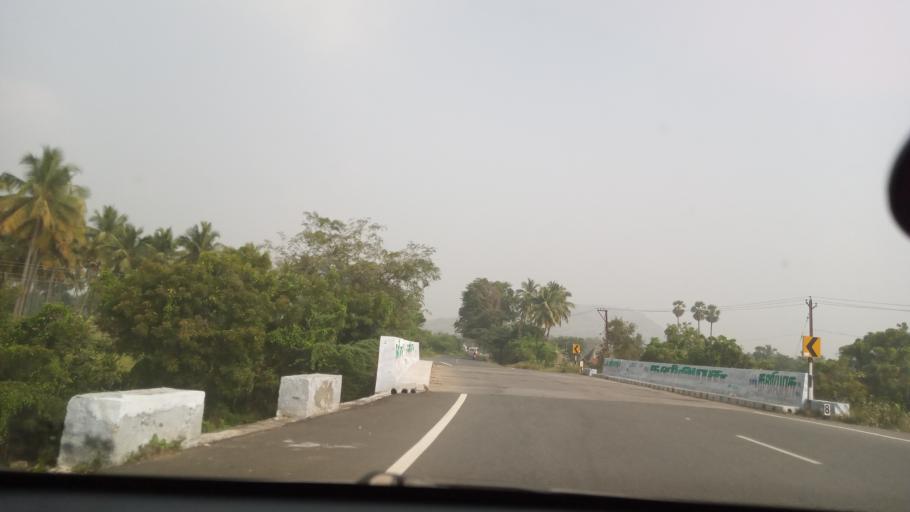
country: IN
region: Tamil Nadu
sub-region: Erode
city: Punjai Puliyampatti
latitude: 11.3210
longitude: 77.1483
